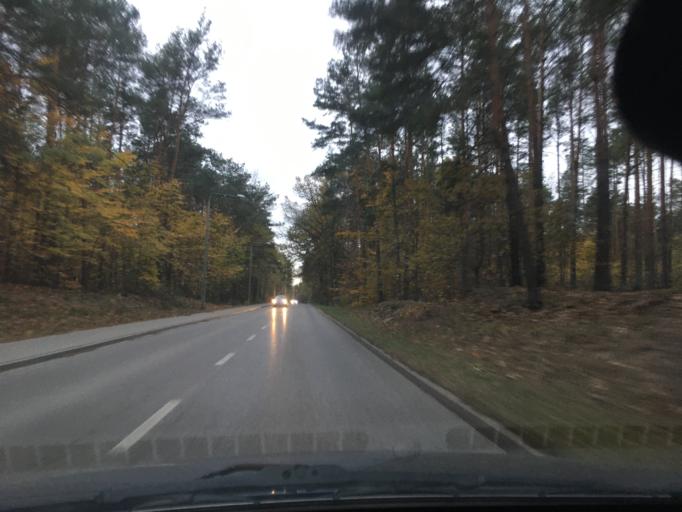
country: PL
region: Masovian Voivodeship
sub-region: Powiat piaseczynski
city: Lesznowola
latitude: 52.0812
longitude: 20.9388
